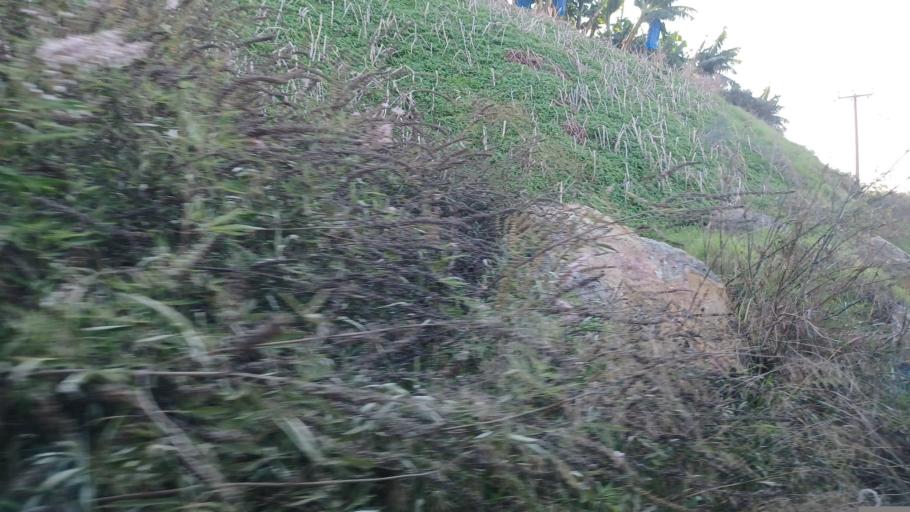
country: CY
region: Pafos
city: Kissonerga
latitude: 34.8352
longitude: 32.3949
